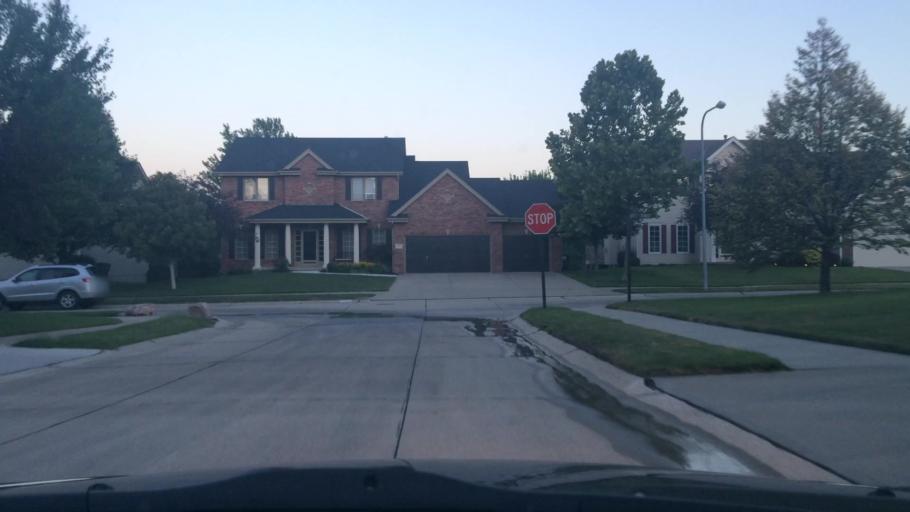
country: US
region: Nebraska
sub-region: Sarpy County
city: La Vista
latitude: 41.1821
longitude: -96.0576
